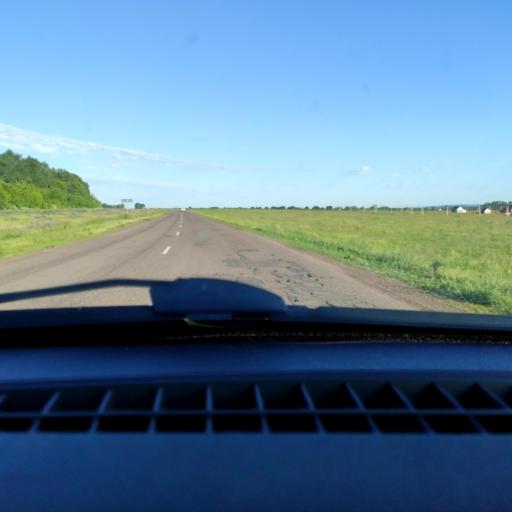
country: RU
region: Bashkortostan
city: Kabakovo
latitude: 54.4689
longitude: 56.2253
